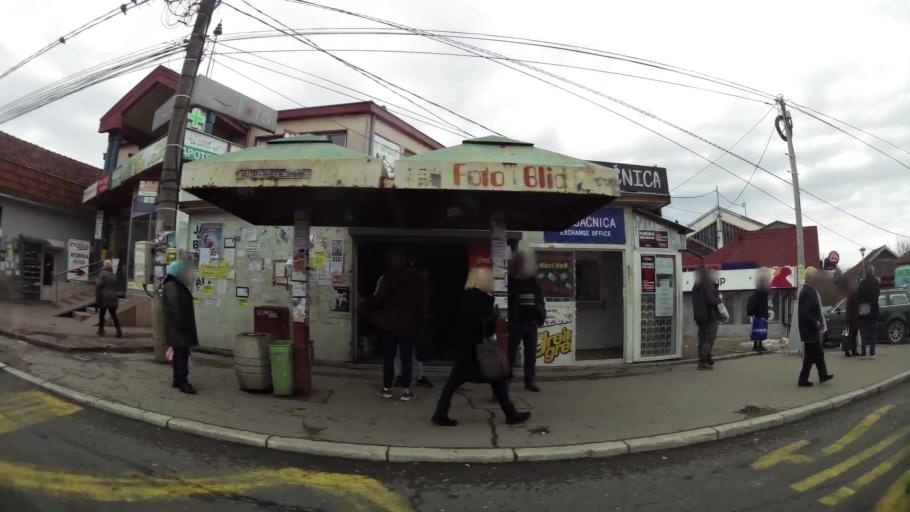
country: RS
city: Ostruznica
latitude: 44.7273
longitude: 20.3685
